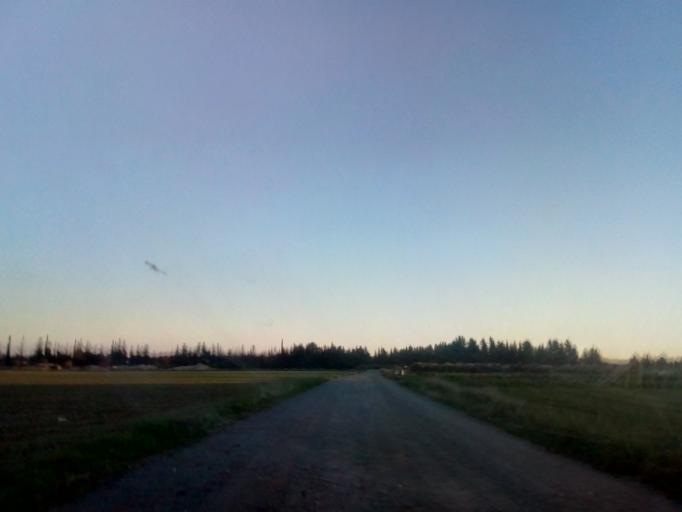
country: CY
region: Limassol
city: Ypsonas
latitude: 34.6709
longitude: 32.9825
